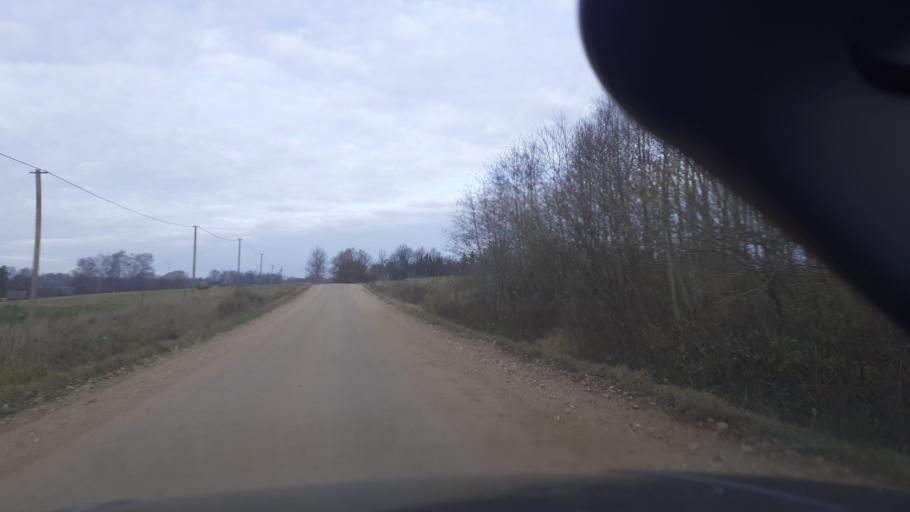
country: LV
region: Alsunga
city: Alsunga
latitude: 56.9061
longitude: 21.6552
